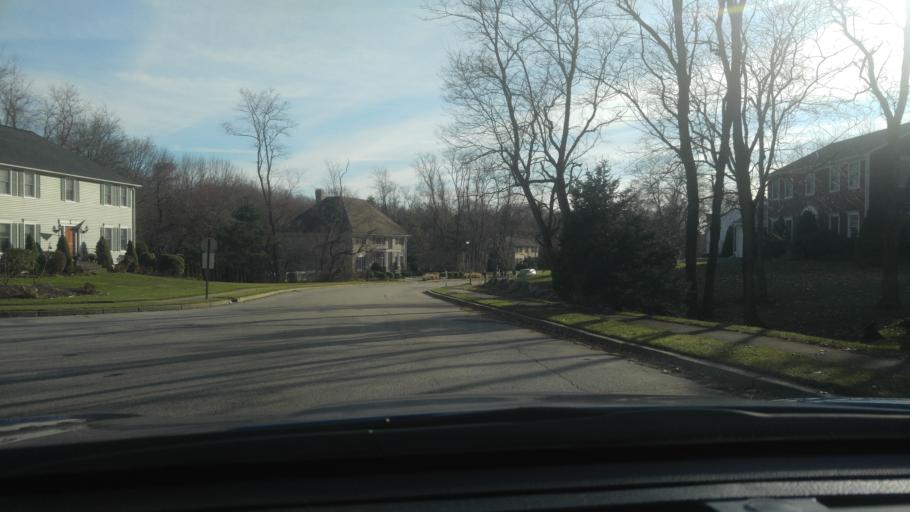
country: US
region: Rhode Island
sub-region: Kent County
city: East Greenwich
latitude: 41.6781
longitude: -71.4695
